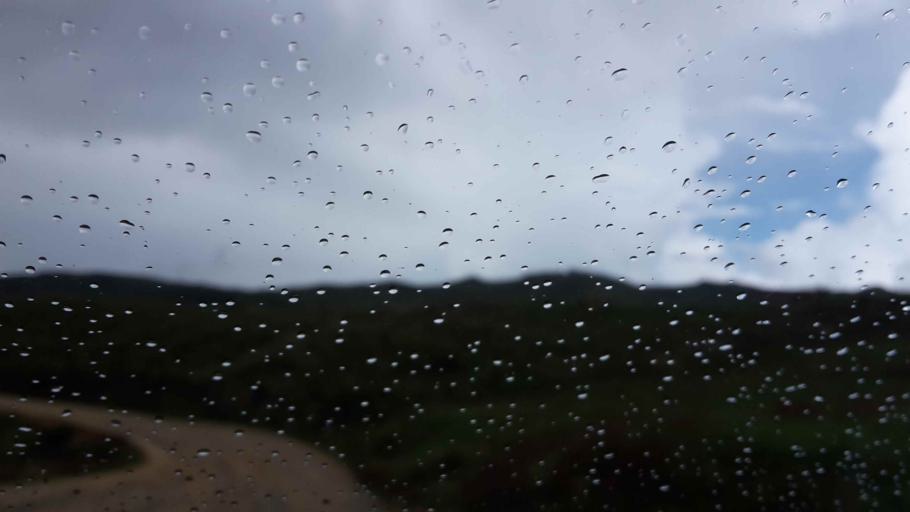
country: BO
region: Cochabamba
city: Cochabamba
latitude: -17.1393
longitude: -66.1062
